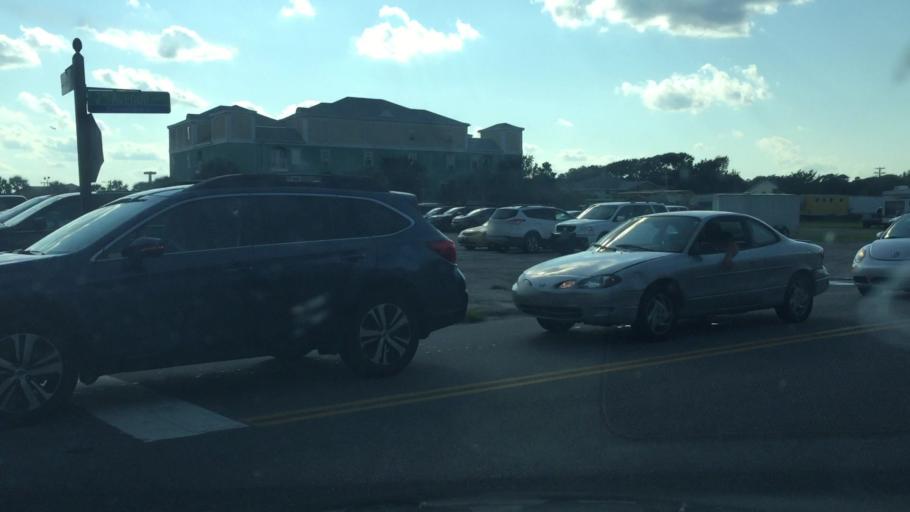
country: US
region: South Carolina
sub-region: Horry County
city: North Myrtle Beach
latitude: 33.8197
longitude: -78.6701
